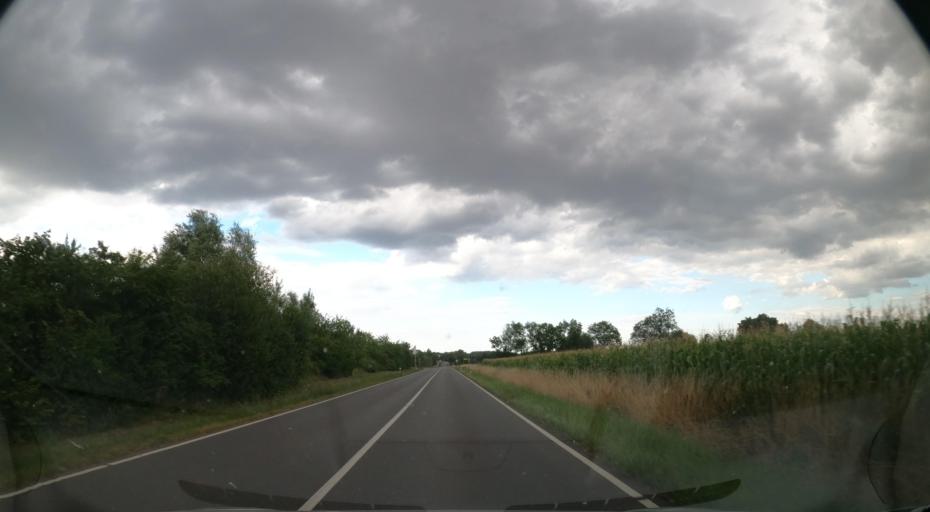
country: DE
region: Mecklenburg-Vorpommern
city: Strasburg
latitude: 53.5008
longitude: 13.7336
